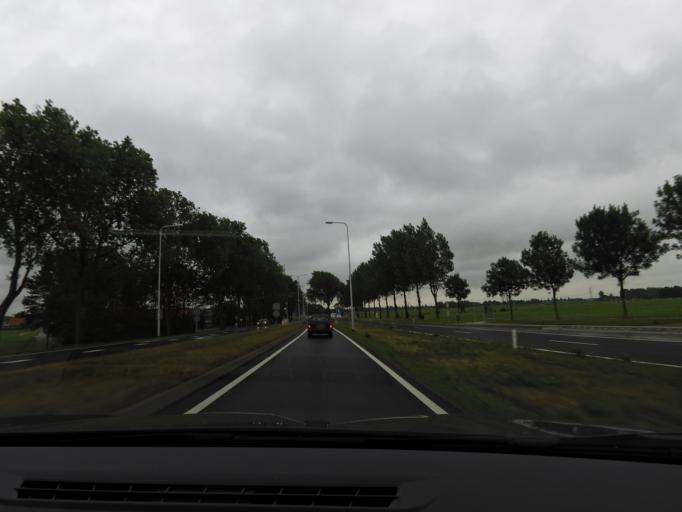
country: NL
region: South Holland
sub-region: Gemeente Maassluis
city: Maassluis
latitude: 51.8659
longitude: 4.2268
